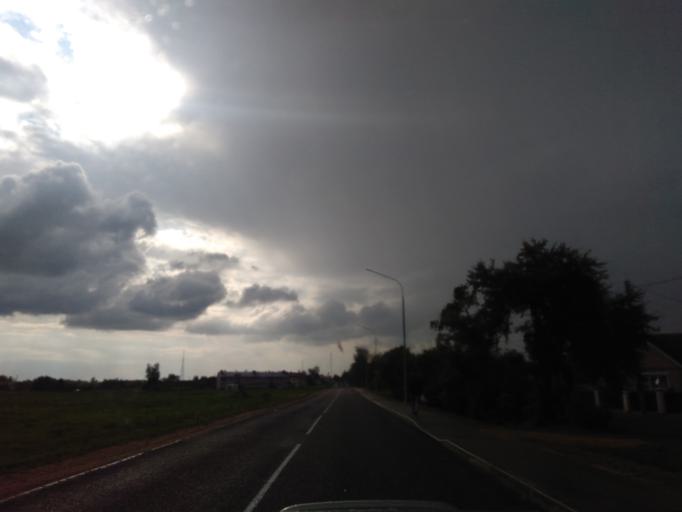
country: BY
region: Minsk
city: Kapyl'
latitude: 53.1422
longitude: 27.1119
